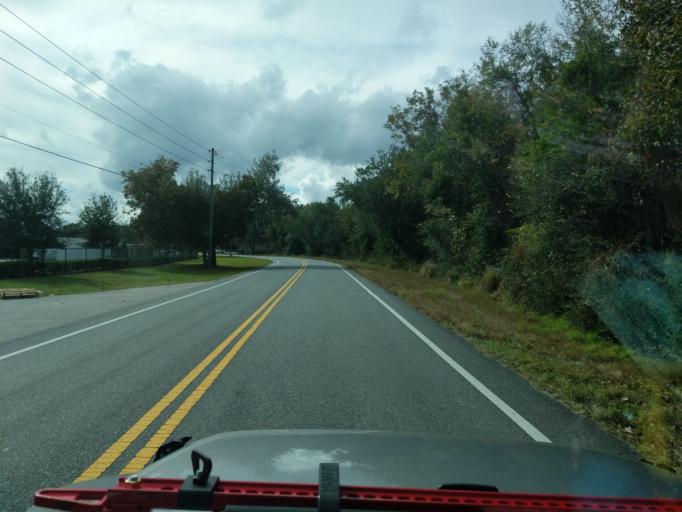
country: US
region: Florida
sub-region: Lake County
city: Clermont
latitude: 28.5719
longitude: -81.8032
